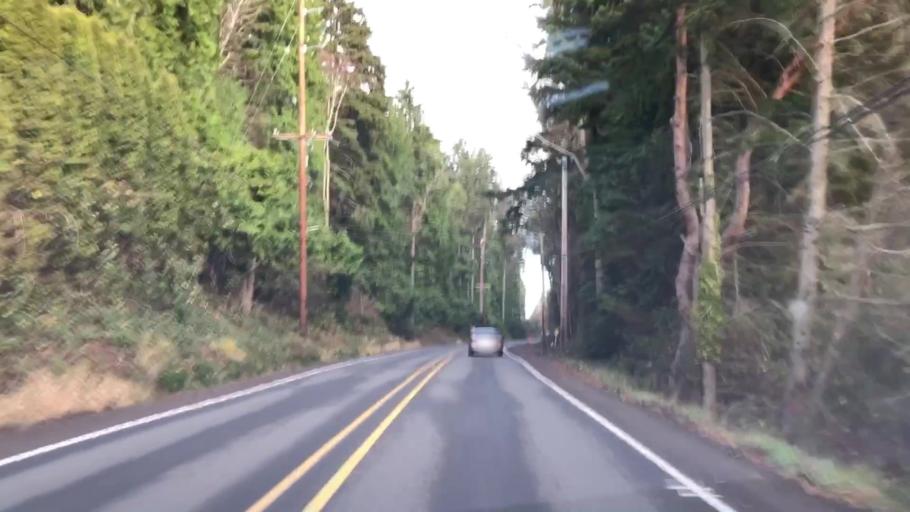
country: US
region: Washington
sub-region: Kitsap County
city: Suquamish
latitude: 47.7517
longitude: -122.5628
